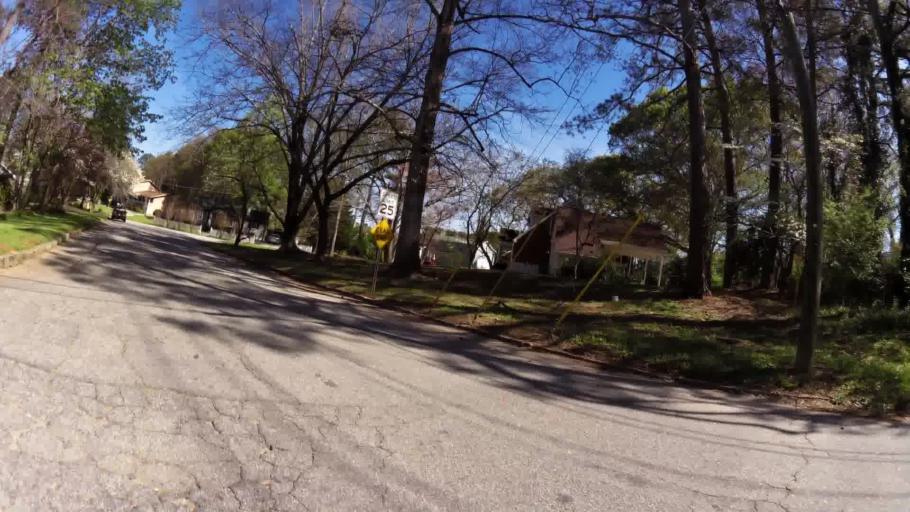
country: US
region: Georgia
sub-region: DeKalb County
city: Clarkston
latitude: 33.8263
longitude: -84.2581
